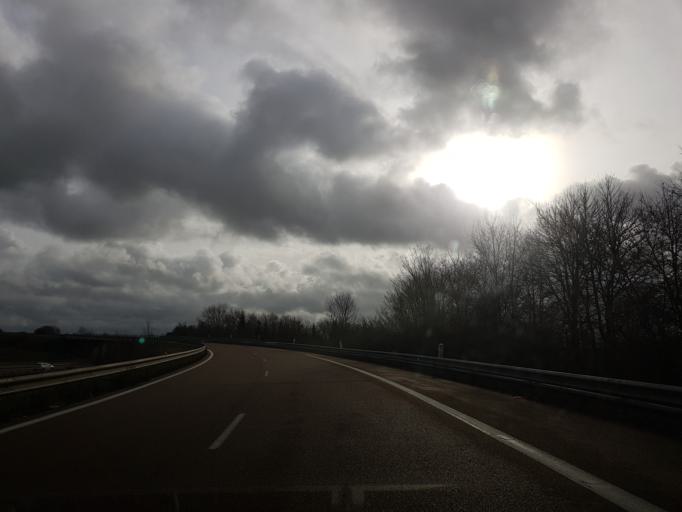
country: FR
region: Champagne-Ardenne
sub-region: Departement de la Haute-Marne
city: Rolampont
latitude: 47.9113
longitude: 5.2214
